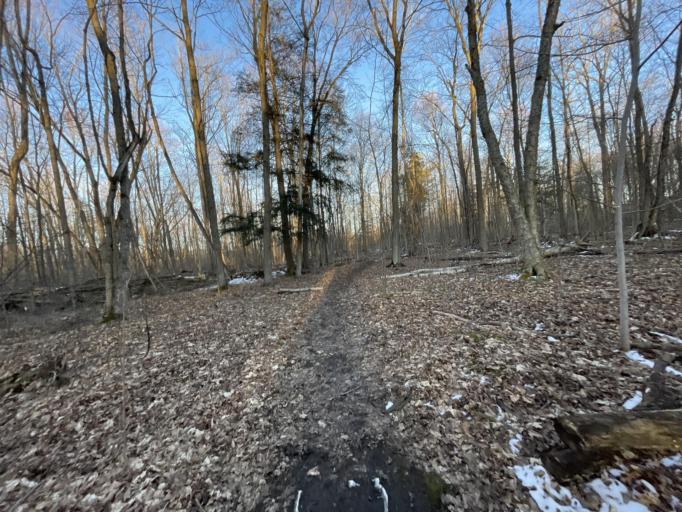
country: CA
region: Ontario
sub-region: Wellington County
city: Guelph
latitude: 43.5250
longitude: -80.3064
